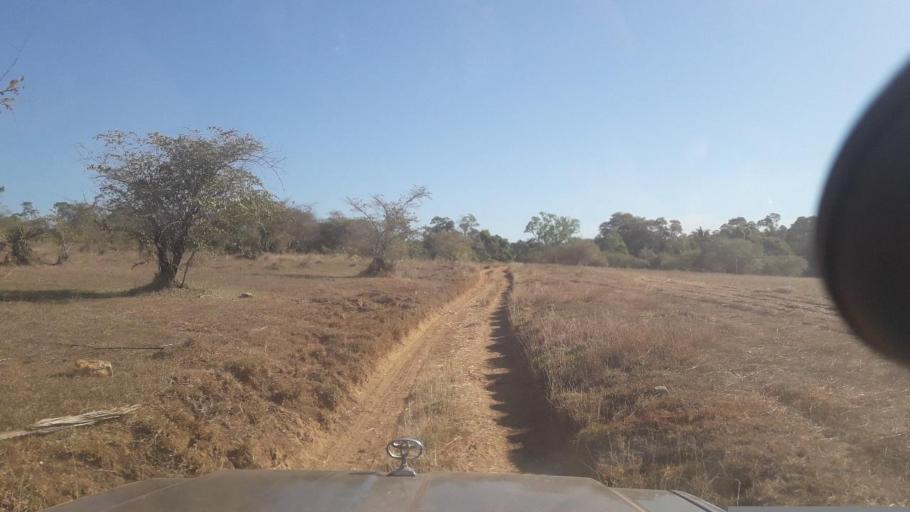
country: MG
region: Boeny
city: Sitampiky
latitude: -16.3763
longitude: 45.5893
